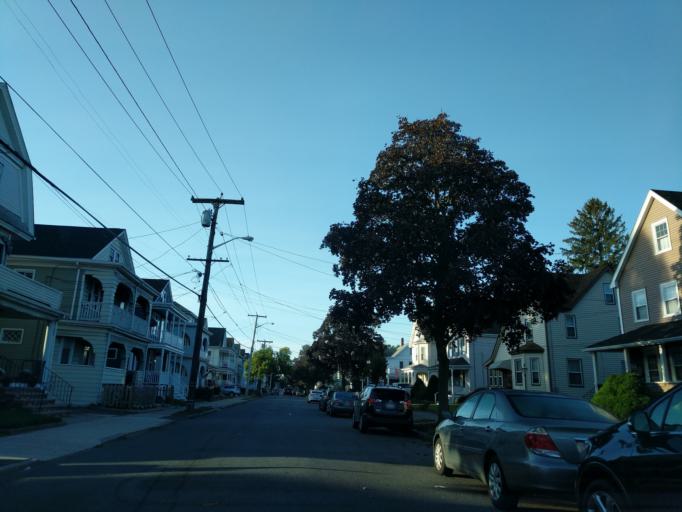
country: US
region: Massachusetts
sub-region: Middlesex County
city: Medford
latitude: 42.4213
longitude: -71.0917
